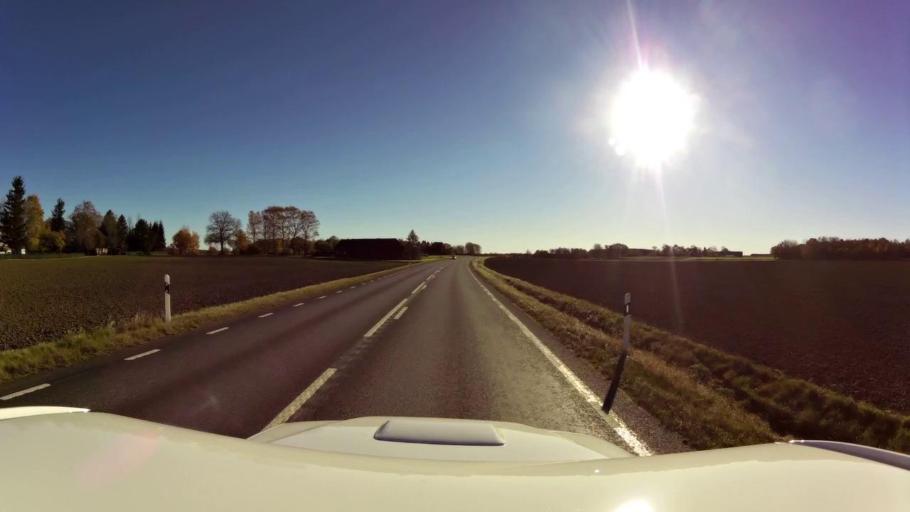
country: SE
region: OEstergoetland
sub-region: Linkopings Kommun
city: Ljungsbro
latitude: 58.5267
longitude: 15.4129
